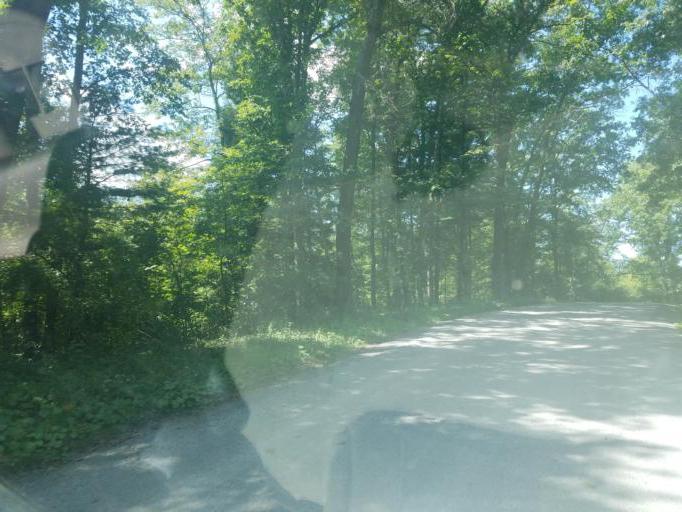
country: US
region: Pennsylvania
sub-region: Clarion County
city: Clarion
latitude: 41.1687
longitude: -79.4350
